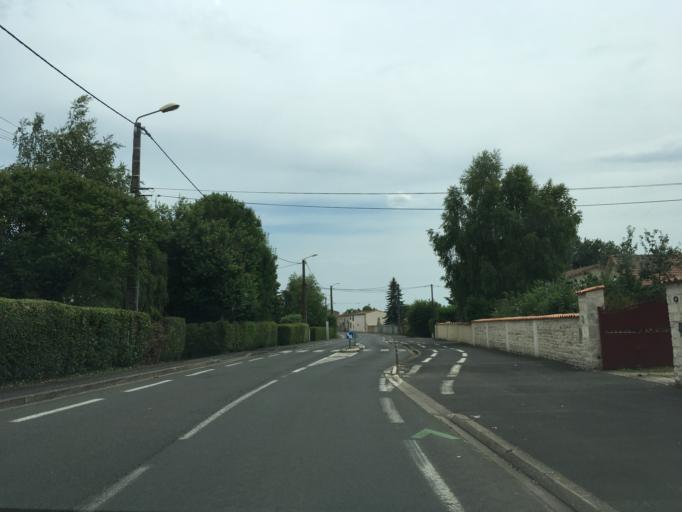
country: FR
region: Poitou-Charentes
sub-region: Departement des Deux-Sevres
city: Bessines
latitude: 46.3185
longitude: -0.5070
